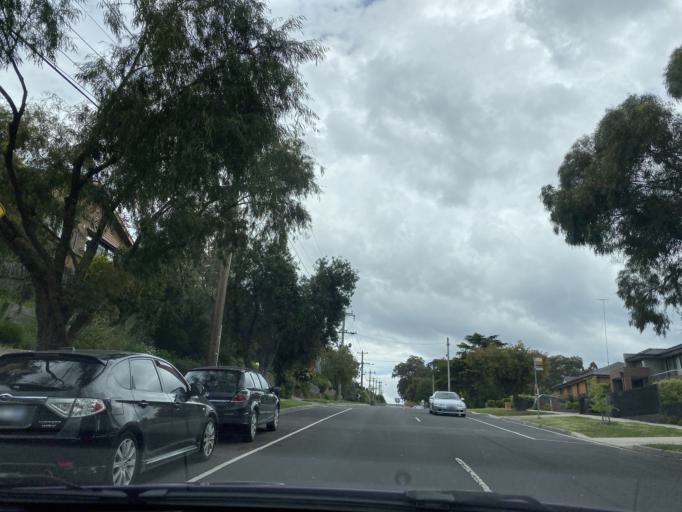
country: AU
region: Victoria
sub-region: Manningham
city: Doncaster East
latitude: -37.7709
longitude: 145.1408
